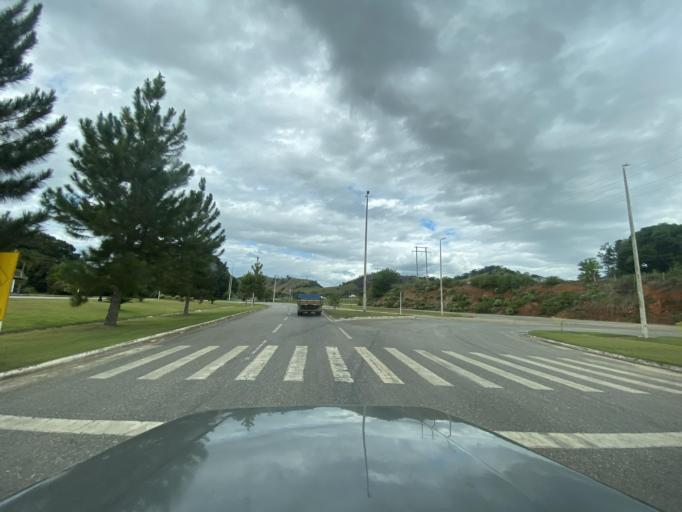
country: BR
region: Espirito Santo
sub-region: Jeronimo Monteiro
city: Jeronimo Monteiro
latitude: -20.7613
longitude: -41.4578
